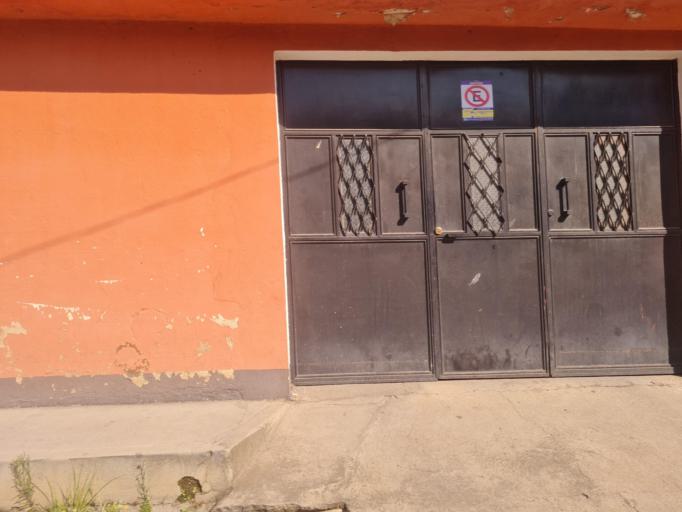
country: GT
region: Quetzaltenango
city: Quetzaltenango
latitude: 14.8409
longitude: -91.5328
